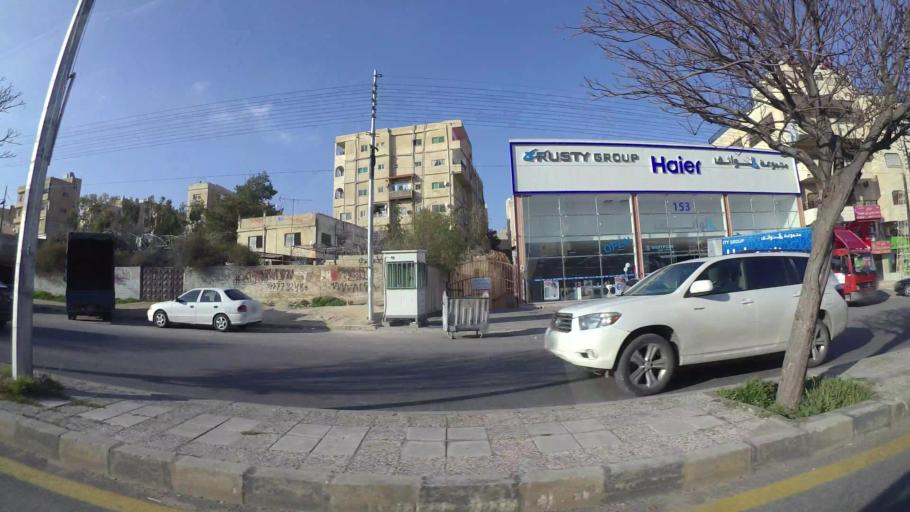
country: JO
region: Amman
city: Amman
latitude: 31.9756
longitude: 35.9578
